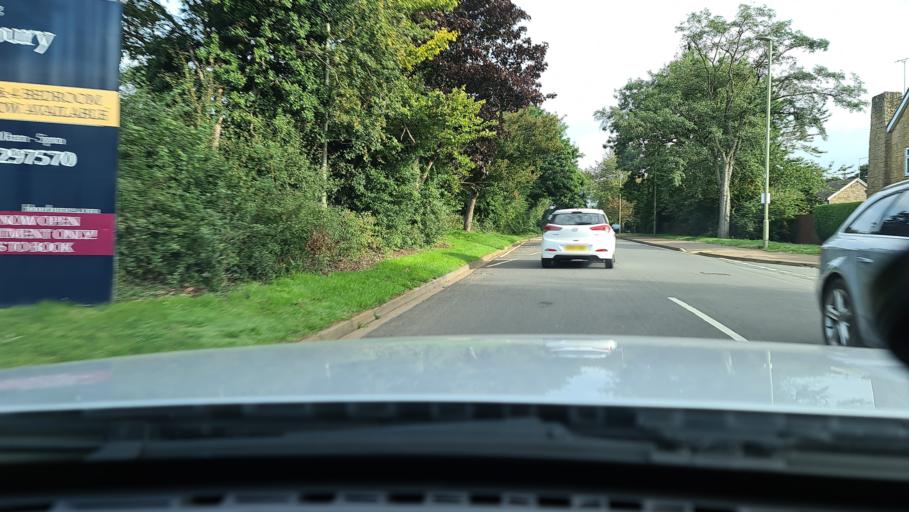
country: GB
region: England
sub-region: Oxfordshire
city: Hanwell
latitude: 52.0698
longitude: -1.3685
